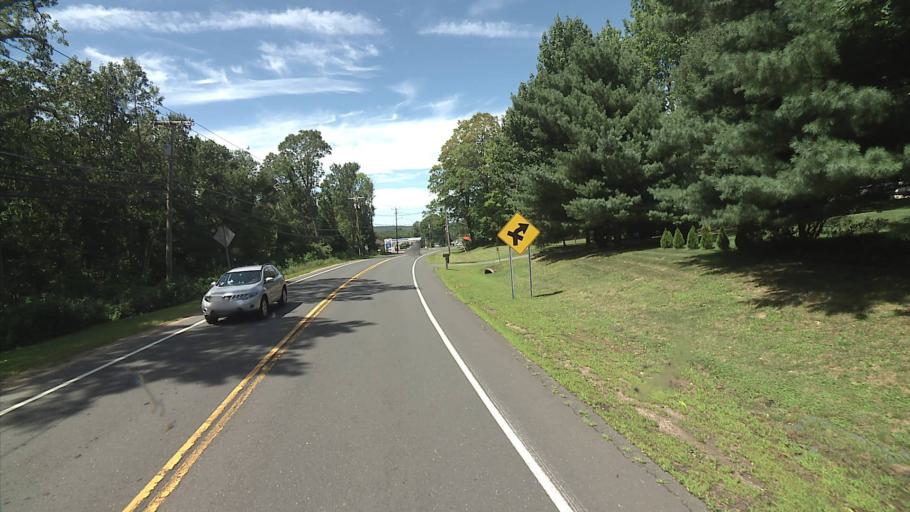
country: US
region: Connecticut
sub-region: Tolland County
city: Tolland
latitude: 41.8523
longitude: -72.3361
